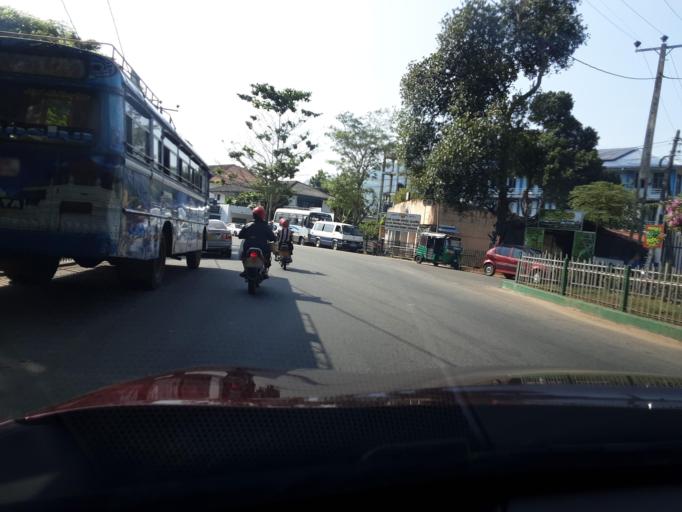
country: LK
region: Uva
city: Badulla
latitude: 6.9878
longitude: 81.0612
